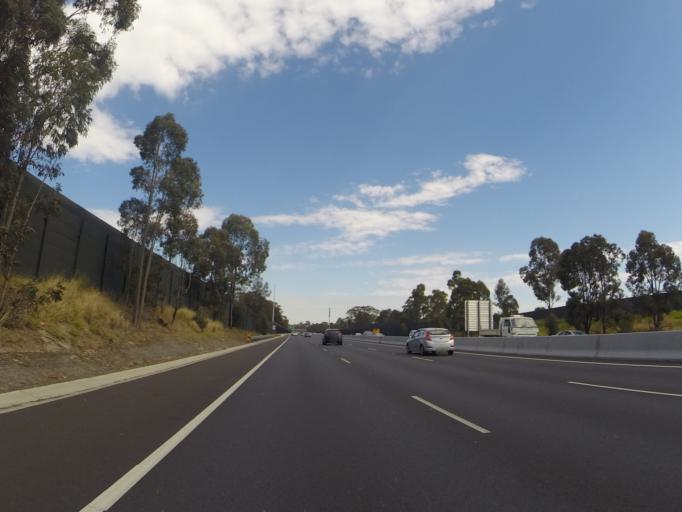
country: AU
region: New South Wales
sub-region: Campbelltown Municipality
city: Glenfield
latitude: -33.9402
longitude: 150.9033
